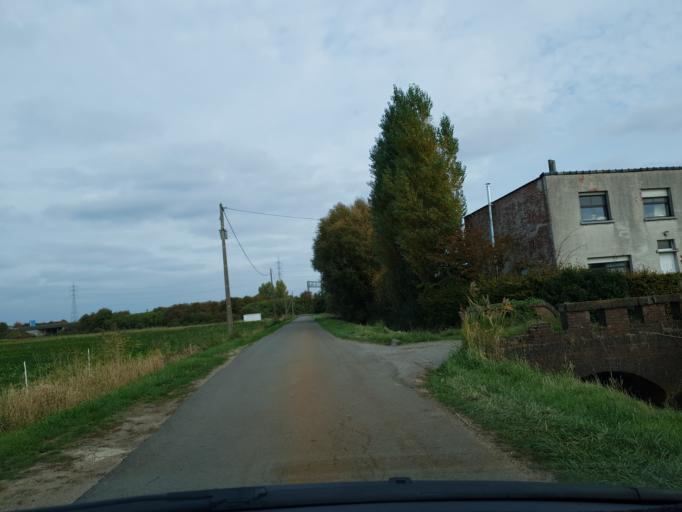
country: BE
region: Flanders
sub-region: Provincie Antwerpen
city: Stabroek
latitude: 51.3416
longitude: 4.3432
